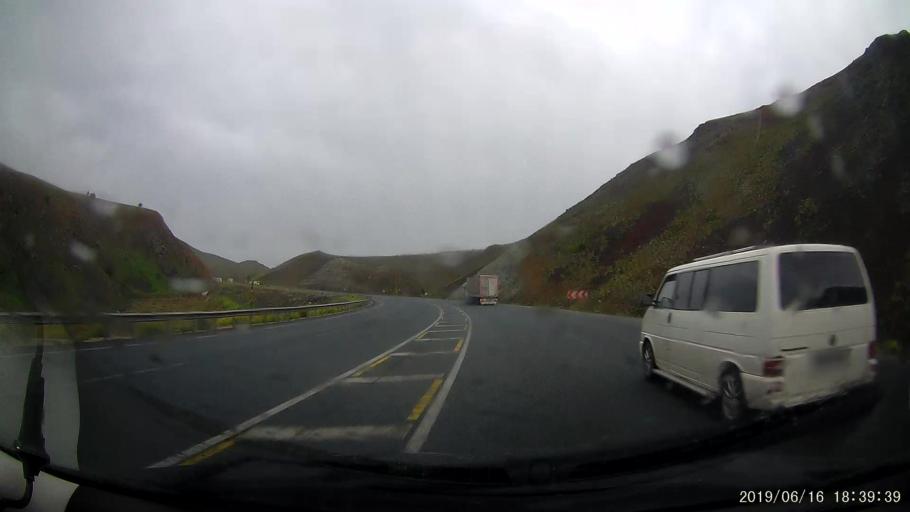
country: TR
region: Erzincan
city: Catalarmut
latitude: 39.8821
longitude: 39.1617
